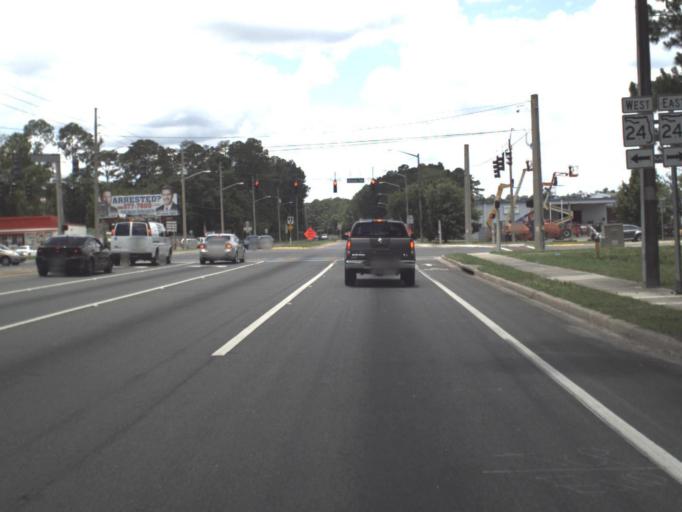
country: US
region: Florida
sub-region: Alachua County
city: Gainesville
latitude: 29.6847
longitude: -82.2885
